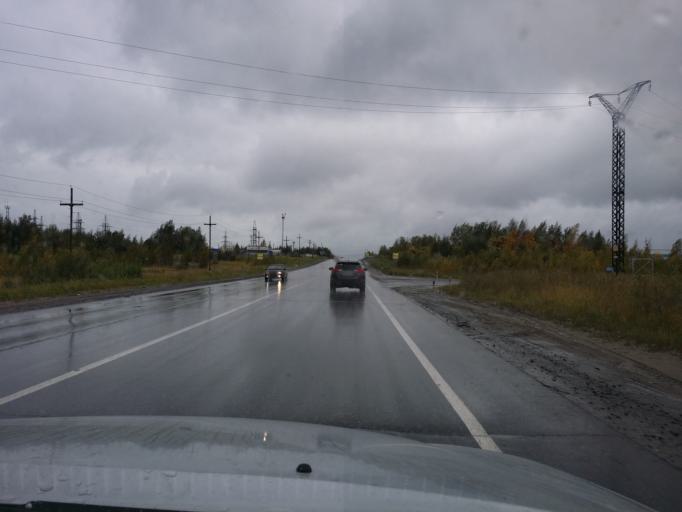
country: RU
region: Khanty-Mansiyskiy Avtonomnyy Okrug
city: Megion
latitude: 61.0582
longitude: 76.1142
